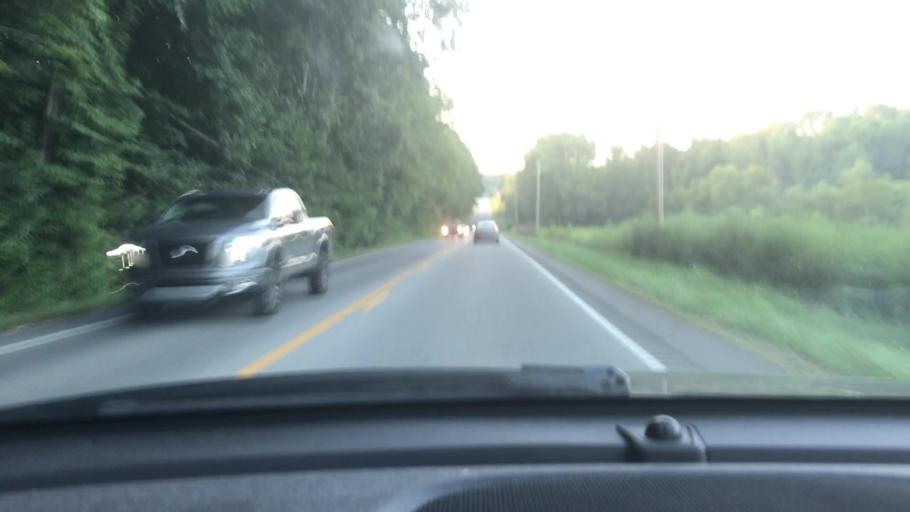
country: US
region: Tennessee
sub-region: Dickson County
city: Dickson
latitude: 36.1253
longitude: -87.3602
